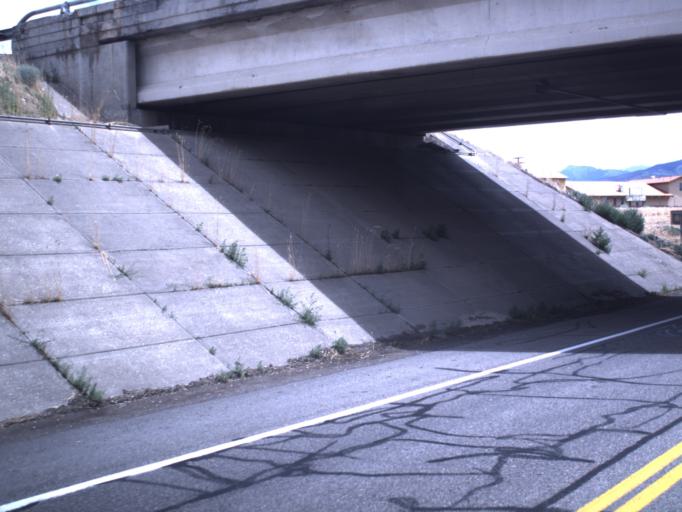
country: US
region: Utah
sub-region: Beaver County
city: Beaver
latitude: 38.2935
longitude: -112.6510
